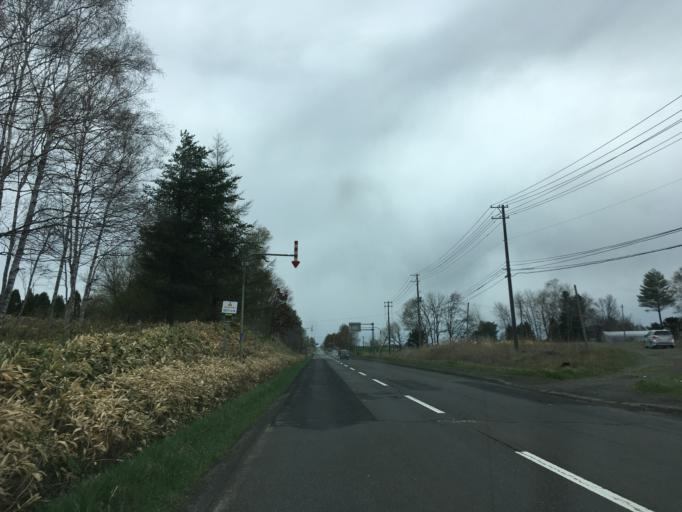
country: JP
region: Hokkaido
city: Chitose
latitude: 42.9119
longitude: 141.8110
